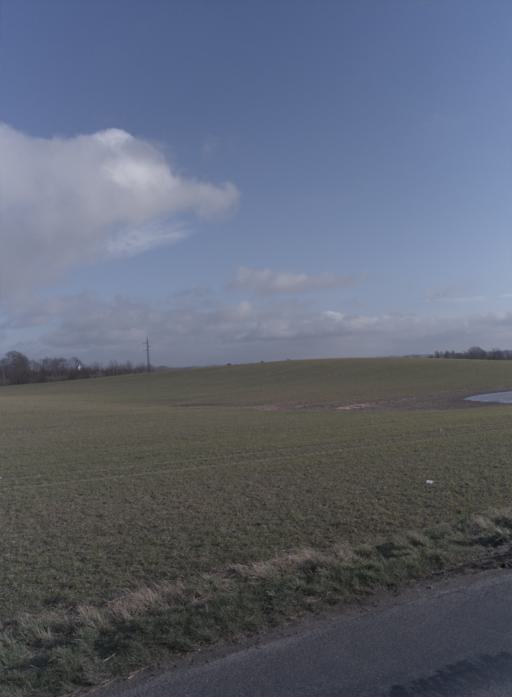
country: DK
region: Zealand
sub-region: Kalundborg Kommune
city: Kalundborg
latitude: 55.6835
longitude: 11.1341
